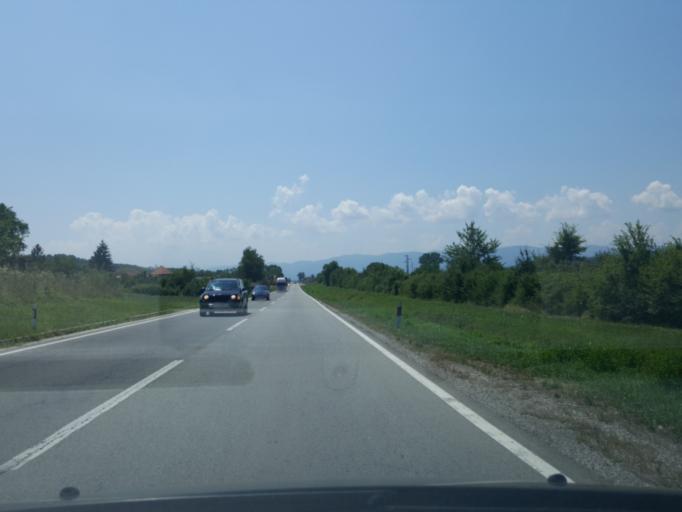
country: RS
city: Prislonica
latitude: 43.9433
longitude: 20.4137
